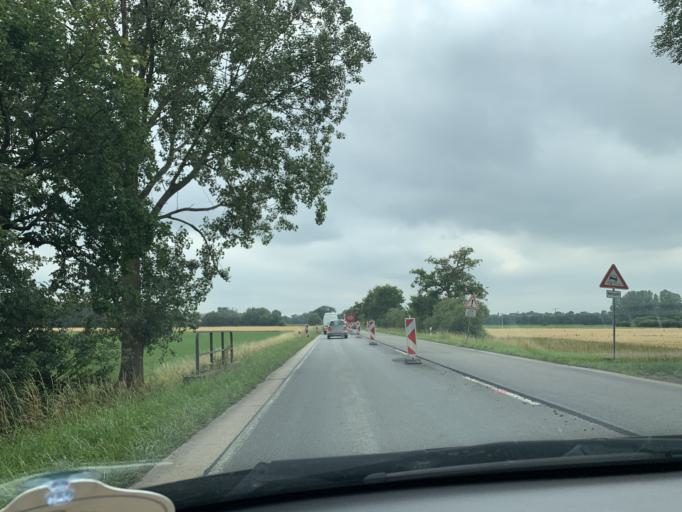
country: DE
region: North Rhine-Westphalia
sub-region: Regierungsbezirk Munster
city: Ennigerloh
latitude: 51.8960
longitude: 8.0521
